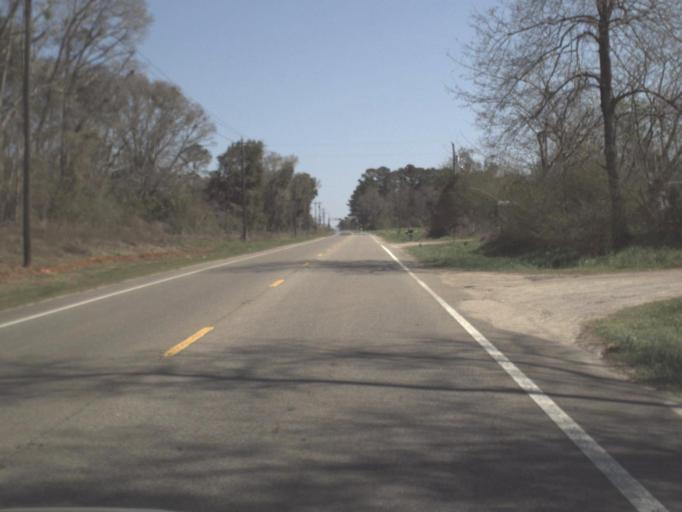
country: US
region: Florida
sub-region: Gadsden County
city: Gretna
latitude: 30.5915
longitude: -84.6492
